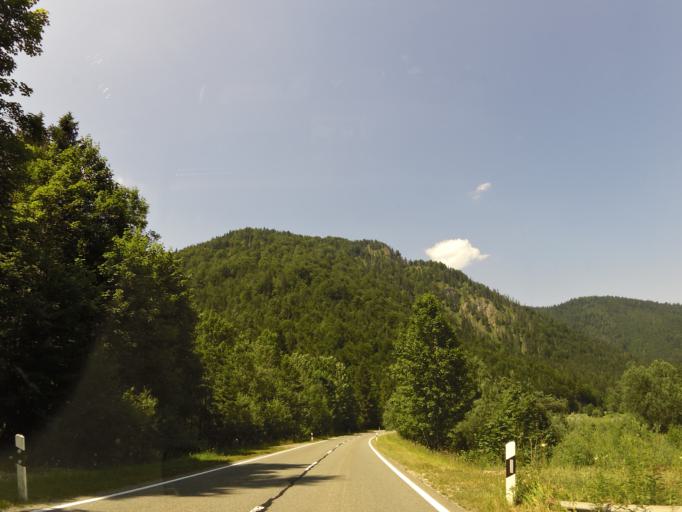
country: DE
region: Bavaria
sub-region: Upper Bavaria
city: Reit im Winkl
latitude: 47.6760
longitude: 12.5462
